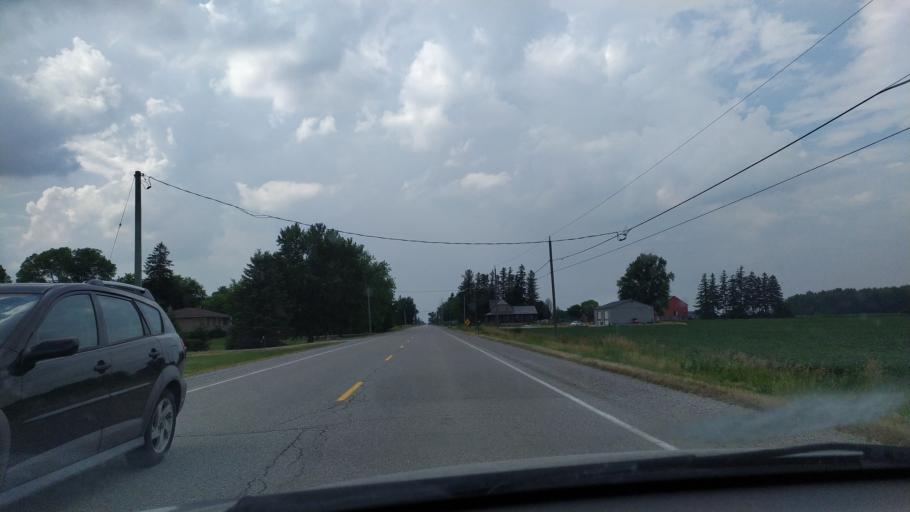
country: CA
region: Ontario
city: Dorchester
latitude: 43.1728
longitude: -81.1384
